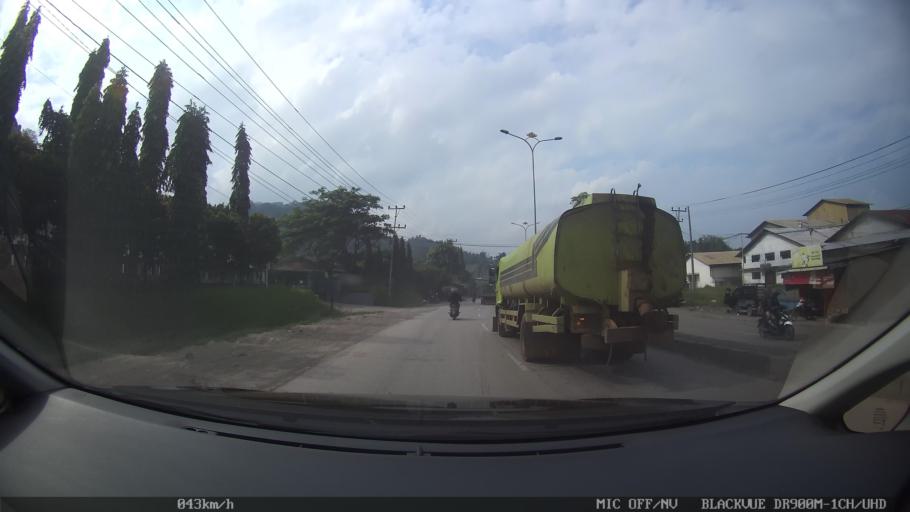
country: ID
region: Lampung
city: Panjang
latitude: -5.4446
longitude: 105.3129
